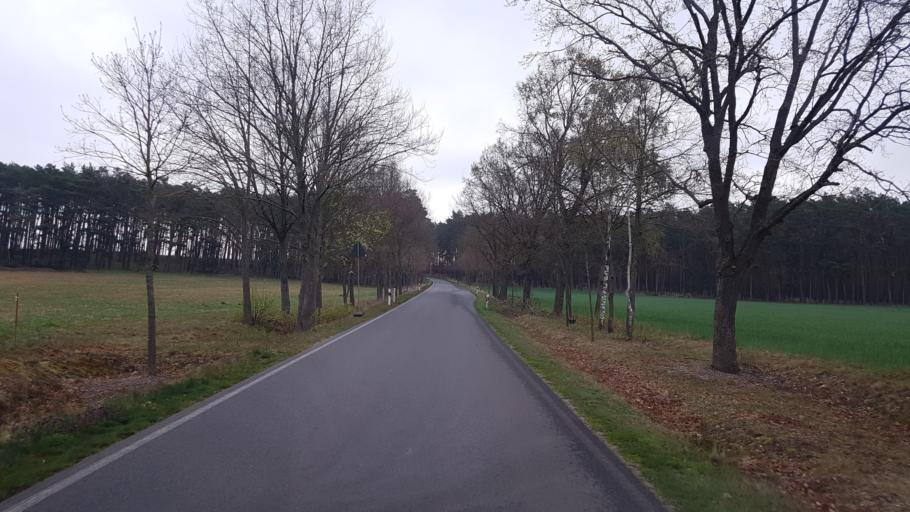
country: DE
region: Brandenburg
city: Drahnsdorf
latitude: 51.9035
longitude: 13.5523
